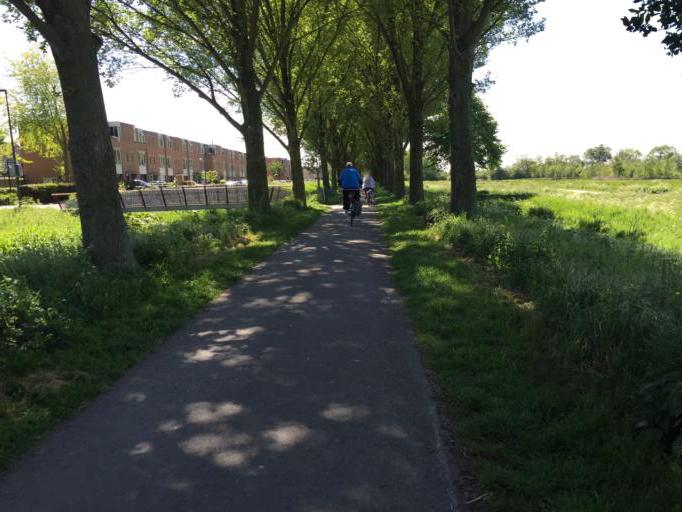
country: NL
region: South Holland
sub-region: Gemeente Schiedam
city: Schiedam
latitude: 51.9483
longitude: 4.3780
